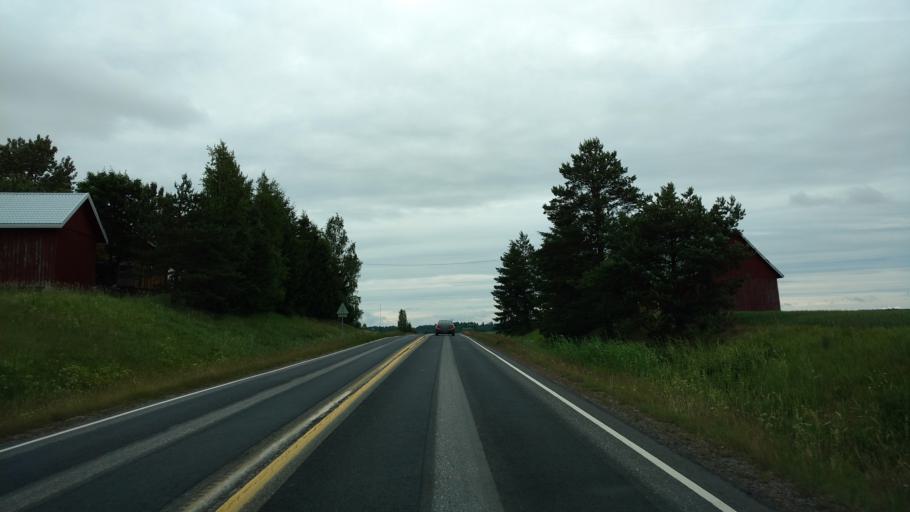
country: FI
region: Varsinais-Suomi
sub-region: Salo
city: Halikko
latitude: 60.4736
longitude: 23.0138
